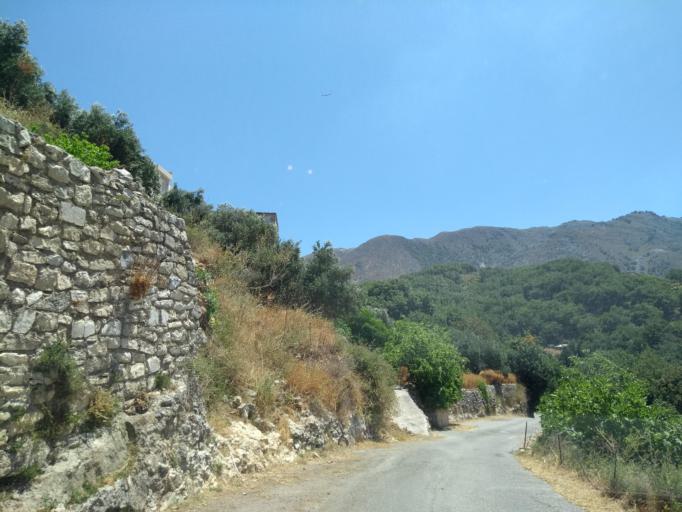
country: GR
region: Crete
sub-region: Nomos Chanias
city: Georgioupolis
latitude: 35.3120
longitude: 24.3092
